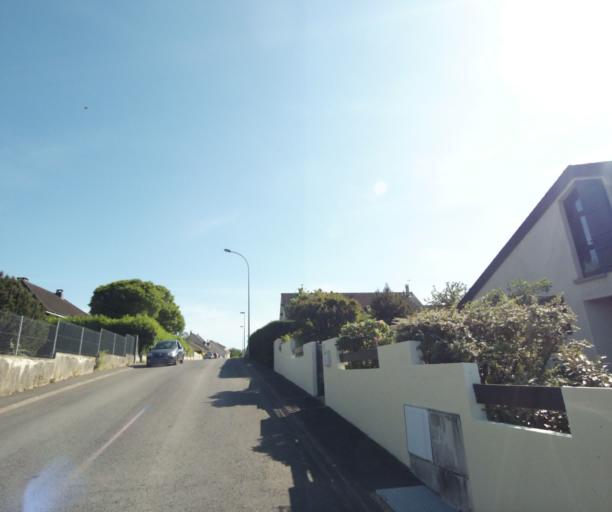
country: FR
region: Champagne-Ardenne
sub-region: Departement des Ardennes
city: Warcq
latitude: 49.7813
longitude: 4.6995
